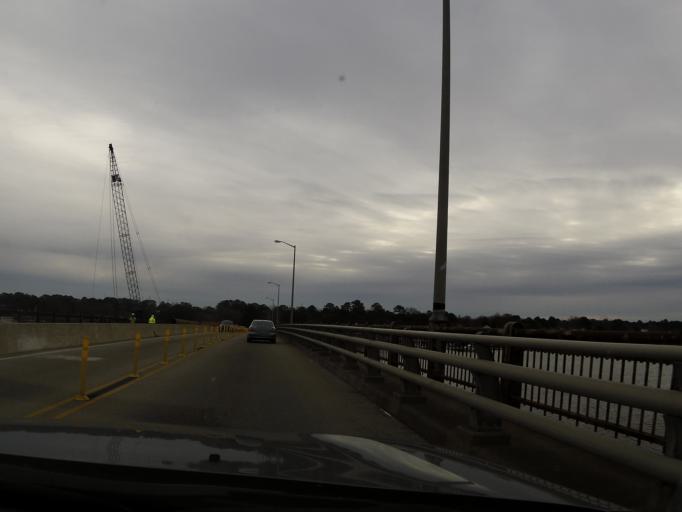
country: US
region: Virginia
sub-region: City of Portsmouth
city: Portsmouth Heights
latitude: 36.8428
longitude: -76.3618
